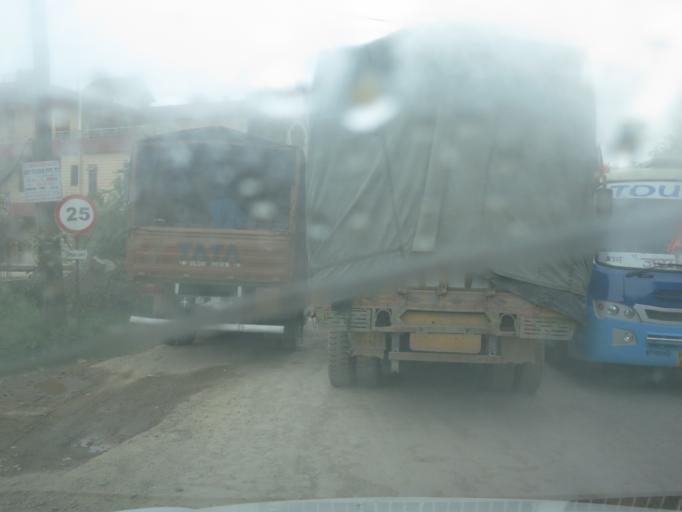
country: IN
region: Himachal Pradesh
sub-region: Mandi
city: Sundarnagar
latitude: 31.5162
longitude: 76.8767
